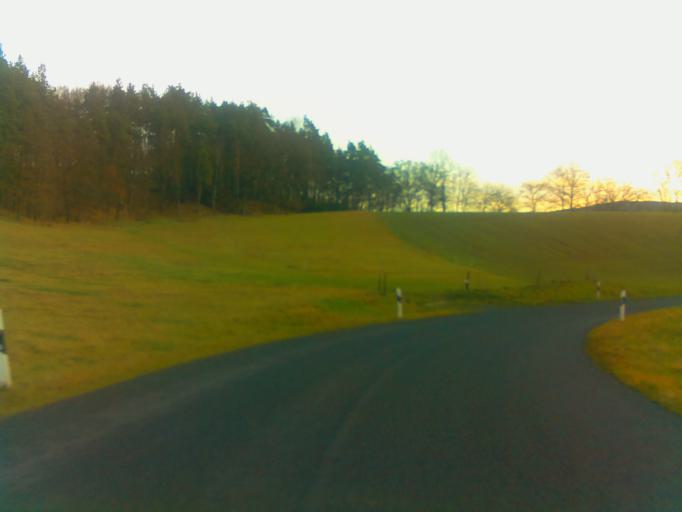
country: DE
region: Thuringia
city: Rudolstadt
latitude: 50.7076
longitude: 11.4025
